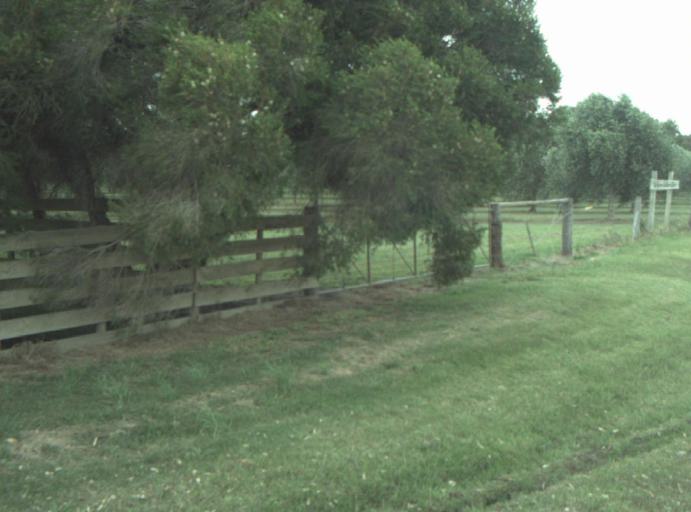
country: AU
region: Victoria
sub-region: Greater Geelong
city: Clifton Springs
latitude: -38.1888
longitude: 144.5783
